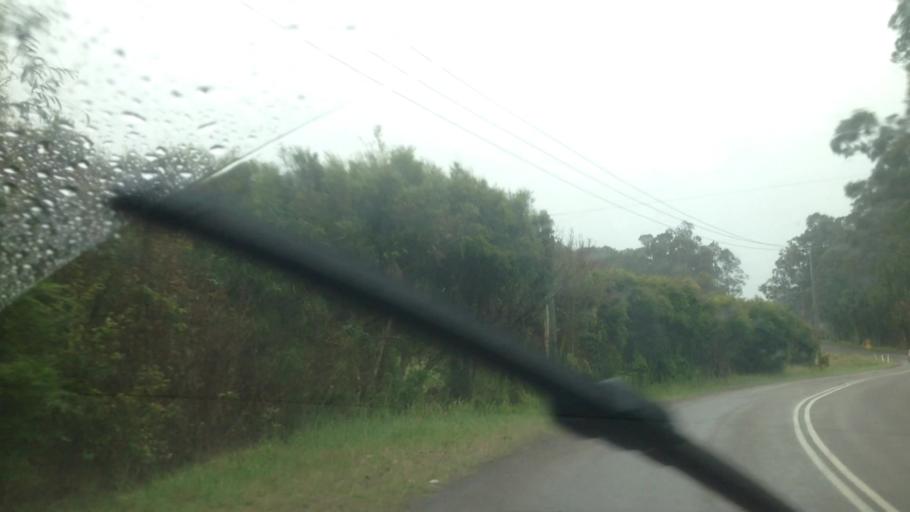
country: AU
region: New South Wales
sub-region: Wyong Shire
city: Little Jilliby
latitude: -33.2164
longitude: 151.3712
